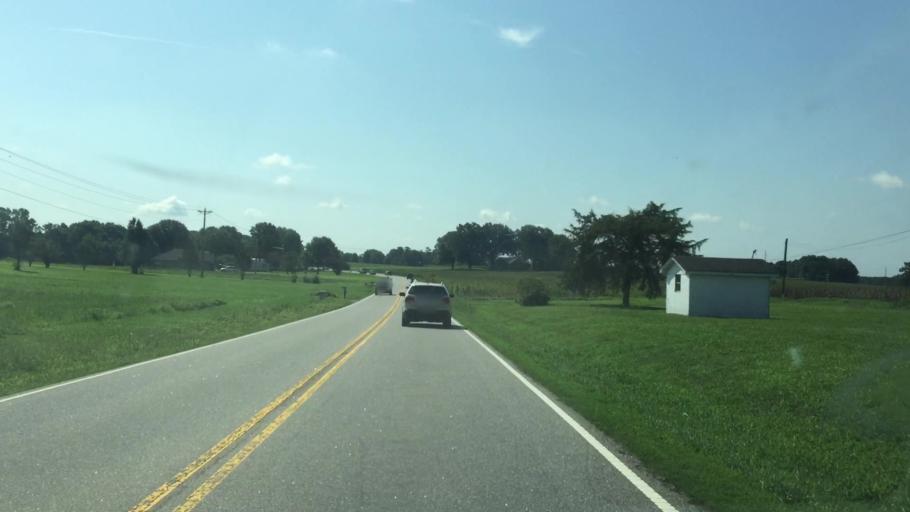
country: US
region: North Carolina
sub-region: Union County
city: Unionville
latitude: 35.1231
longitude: -80.4280
